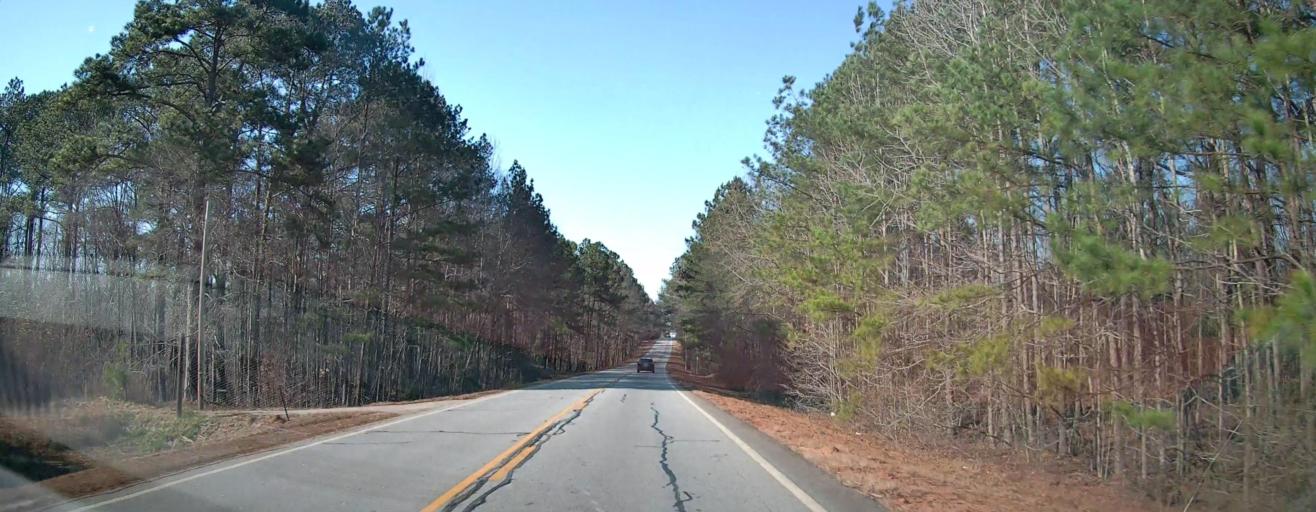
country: US
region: Georgia
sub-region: Butts County
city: Indian Springs
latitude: 33.2288
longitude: -83.8752
